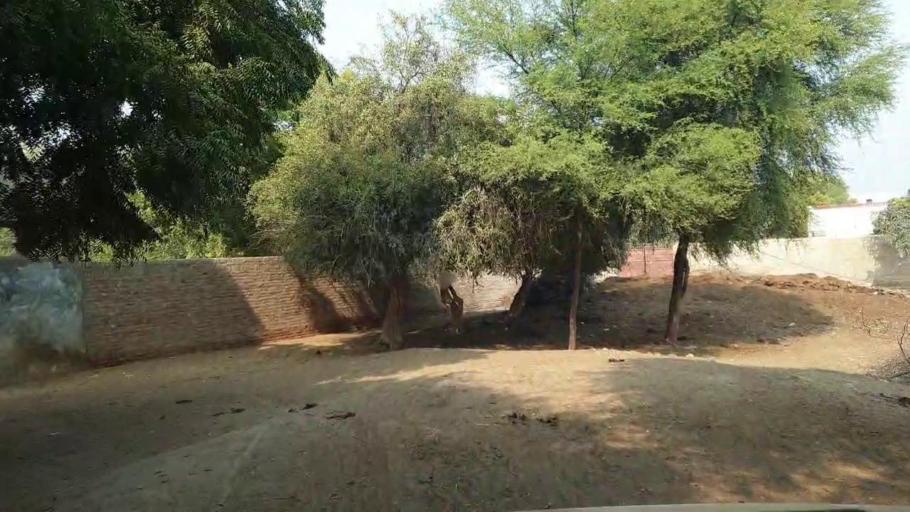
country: PK
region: Sindh
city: Bhit Shah
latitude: 25.8424
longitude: 68.5023
